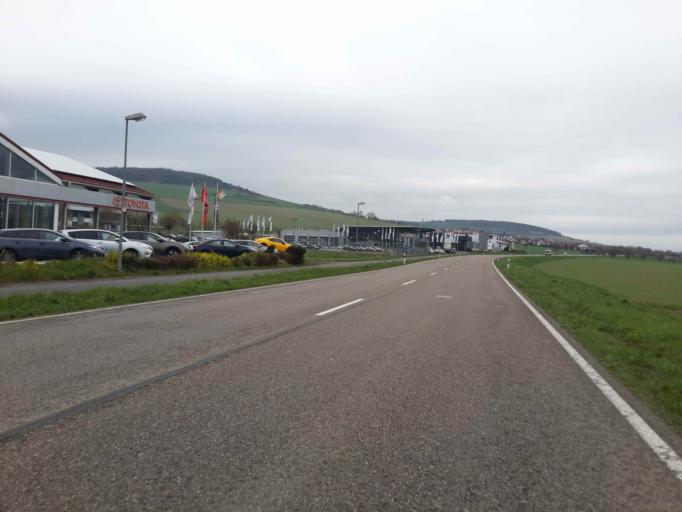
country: DE
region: Baden-Wuerttemberg
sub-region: Regierungsbezirk Stuttgart
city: Lauda-Konigshofen
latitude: 49.5396
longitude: 9.7379
